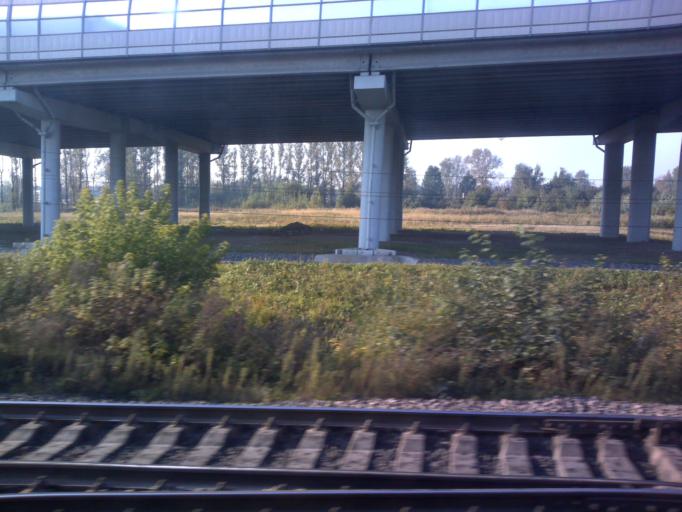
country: RU
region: St.-Petersburg
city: Krasnogvargeisky
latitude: 59.9790
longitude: 30.5277
